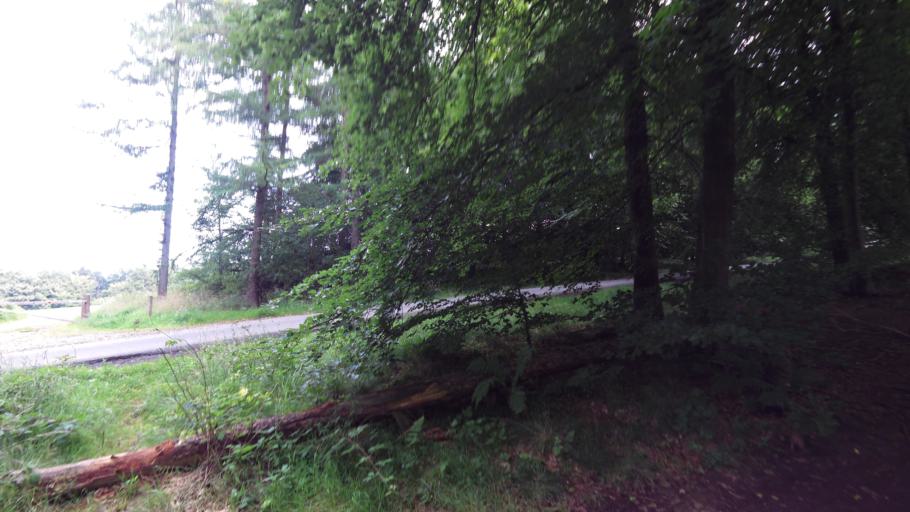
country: GB
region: England
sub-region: North Yorkshire
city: Thornton Dale
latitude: 54.2962
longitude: -0.6453
